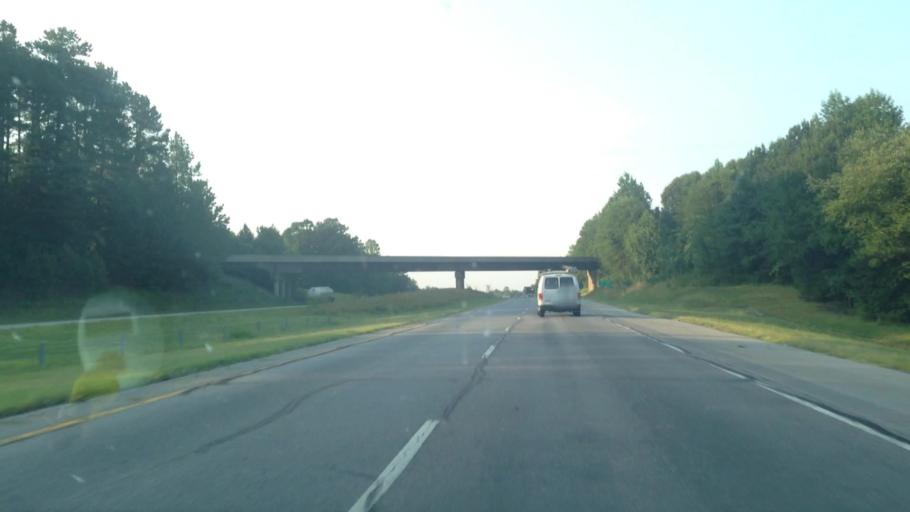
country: US
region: Virginia
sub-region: City of Danville
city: Danville
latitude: 36.5073
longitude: -79.4786
